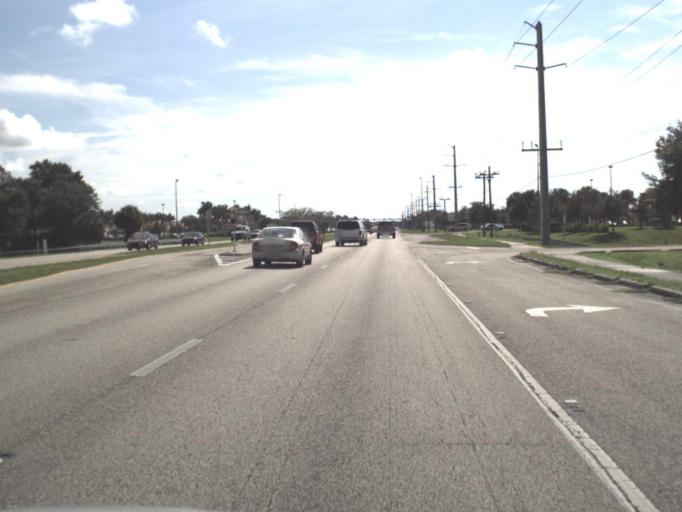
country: US
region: Florida
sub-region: Sarasota County
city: North Port
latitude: 27.0378
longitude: -82.2190
